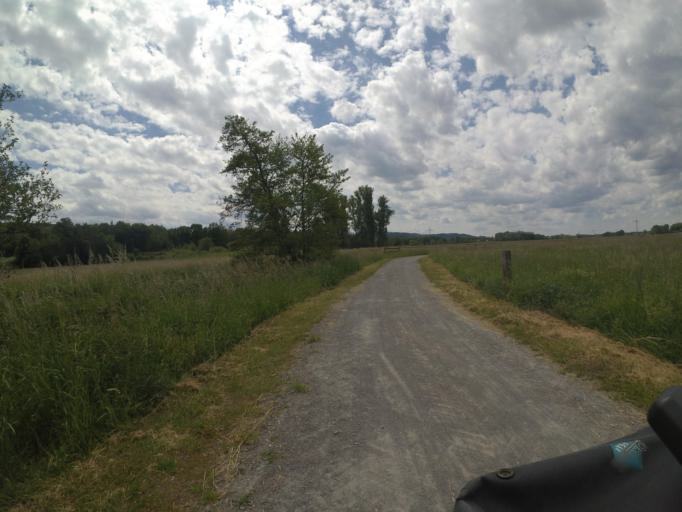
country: DE
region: Rheinland-Pfalz
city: Hauptstuhl
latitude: 49.4016
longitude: 7.4634
